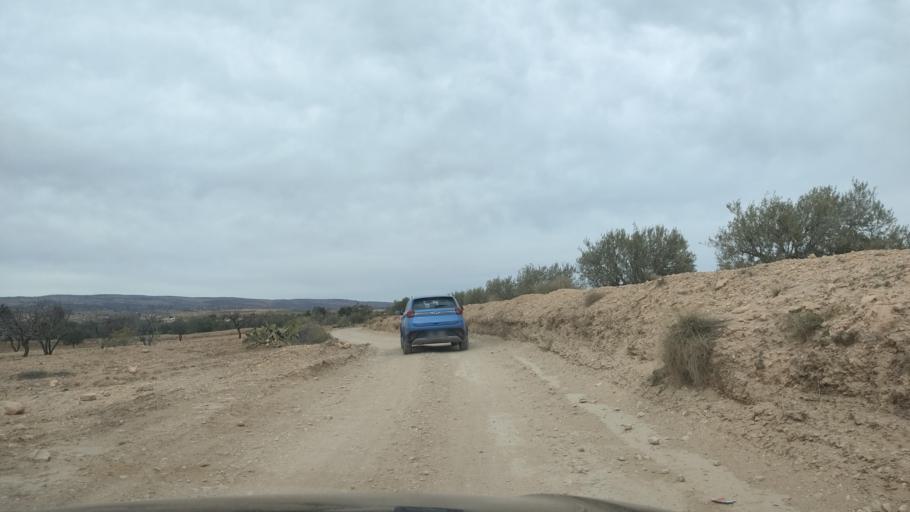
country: TN
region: Al Qasrayn
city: Kasserine
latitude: 35.2537
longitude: 8.9218
